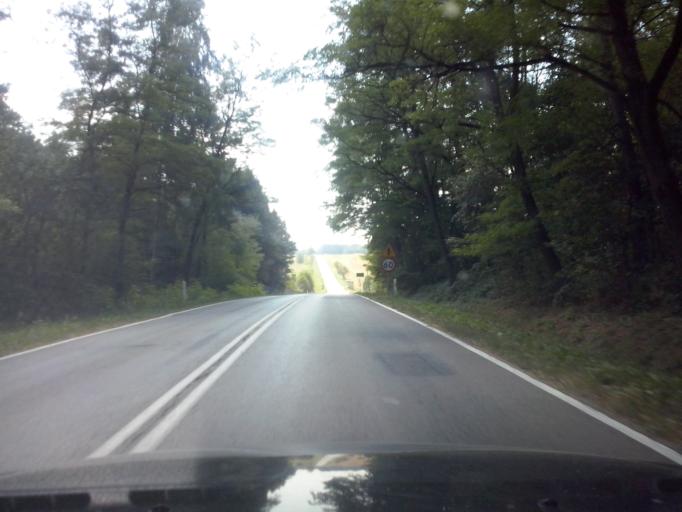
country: PL
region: Swietokrzyskie
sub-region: Powiat kielecki
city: Rakow
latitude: 50.6507
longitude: 21.0268
